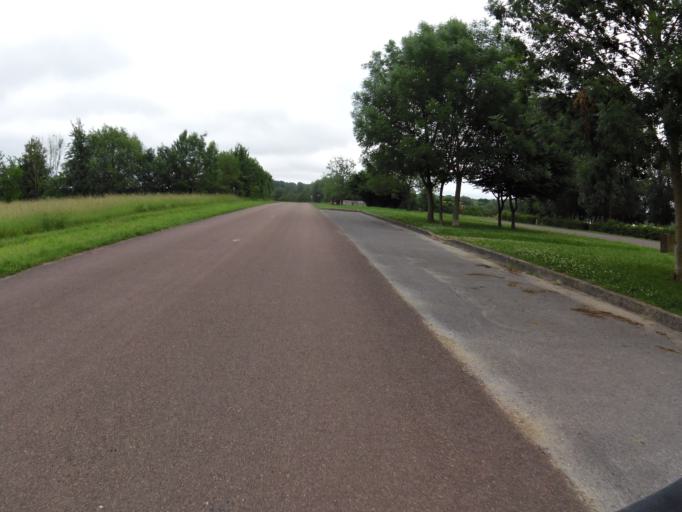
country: FR
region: Champagne-Ardenne
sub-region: Departement de la Haute-Marne
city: Montier-en-Der
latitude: 48.5520
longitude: 4.7937
